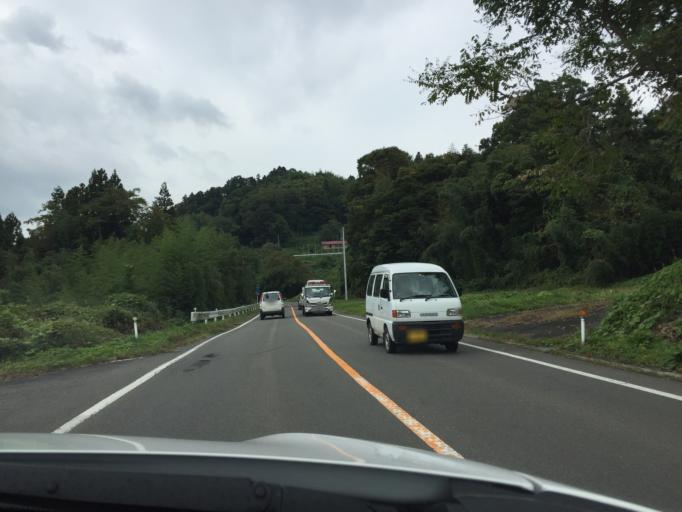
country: JP
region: Fukushima
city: Nihommatsu
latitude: 37.6117
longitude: 140.5356
